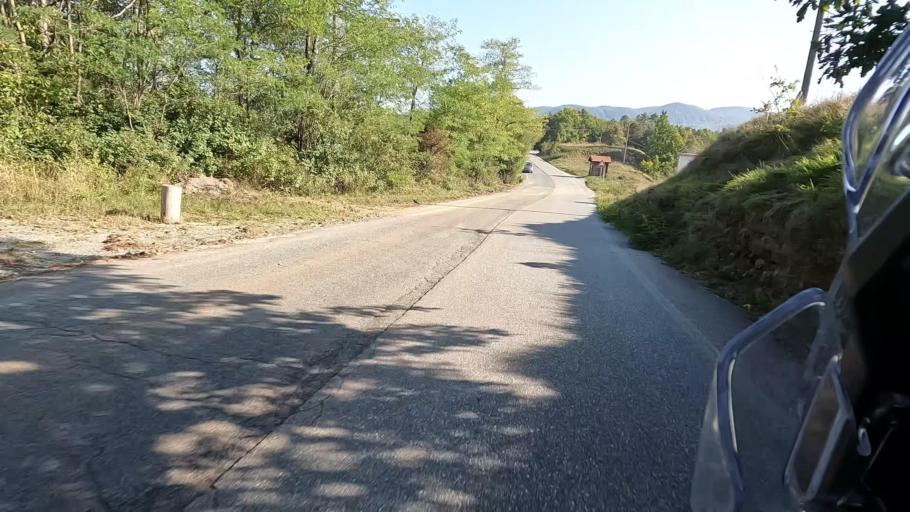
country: IT
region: Liguria
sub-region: Provincia di Savona
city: Urbe
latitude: 44.5011
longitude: 8.5445
